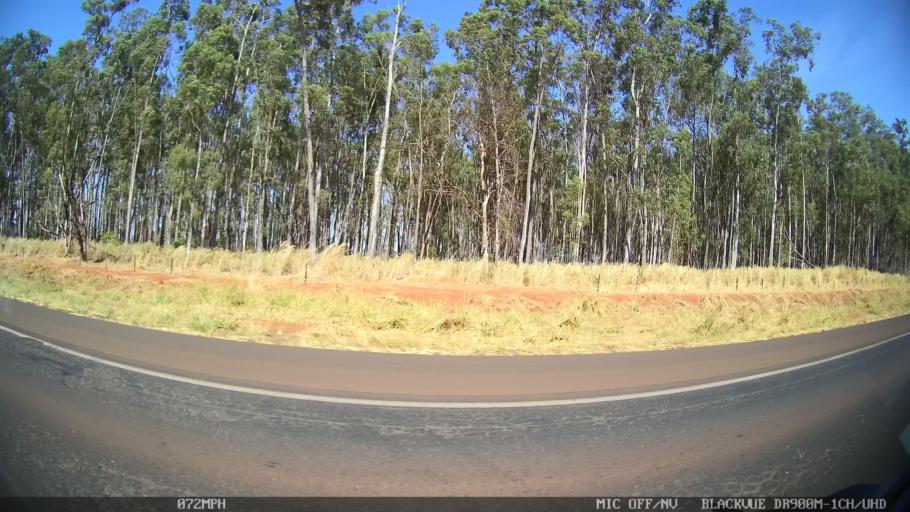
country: BR
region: Sao Paulo
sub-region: Barretos
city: Barretos
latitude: -20.4920
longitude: -48.5246
